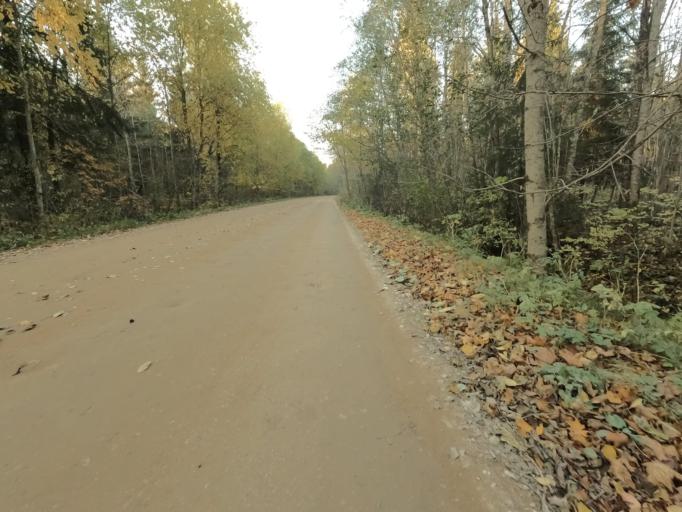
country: RU
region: Leningrad
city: Lyuban'
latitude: 58.9836
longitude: 31.0985
